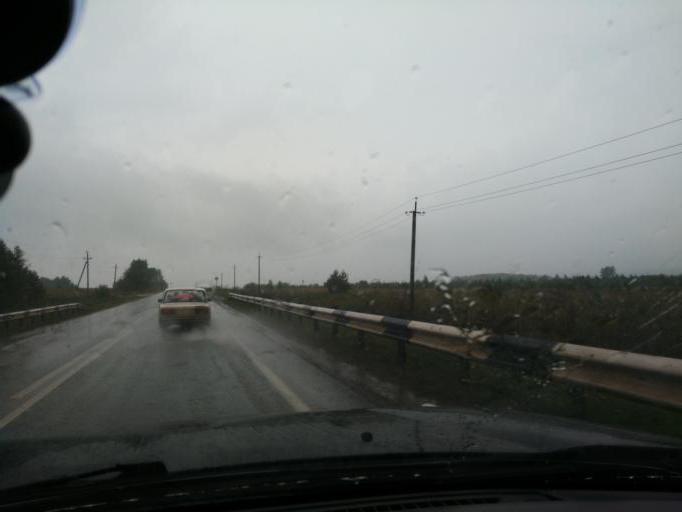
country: RU
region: Perm
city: Osa
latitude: 57.1685
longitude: 55.5316
